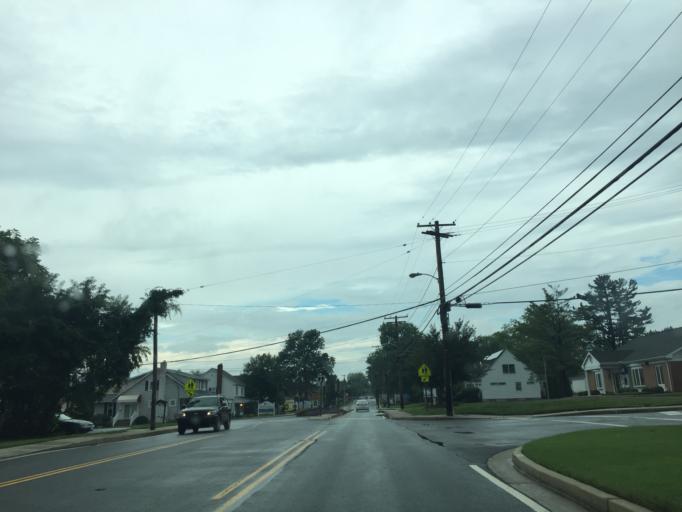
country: US
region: Maryland
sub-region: Harford County
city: South Bel Air
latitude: 39.5311
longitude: -76.3435
